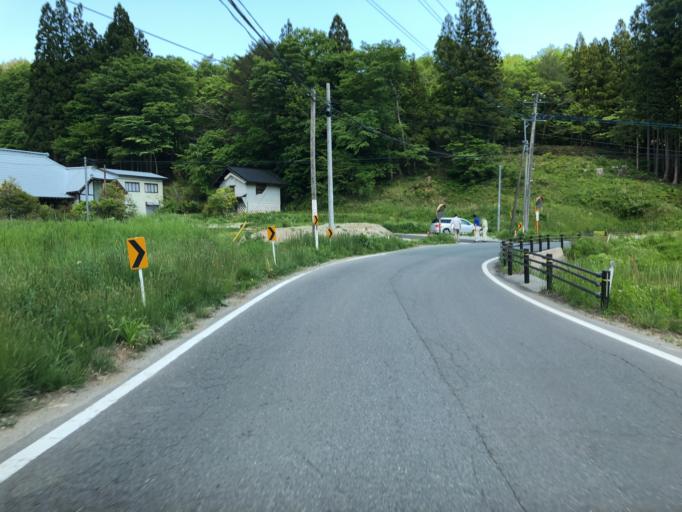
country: JP
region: Fukushima
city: Funehikimachi-funehiki
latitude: 37.5102
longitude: 140.7166
